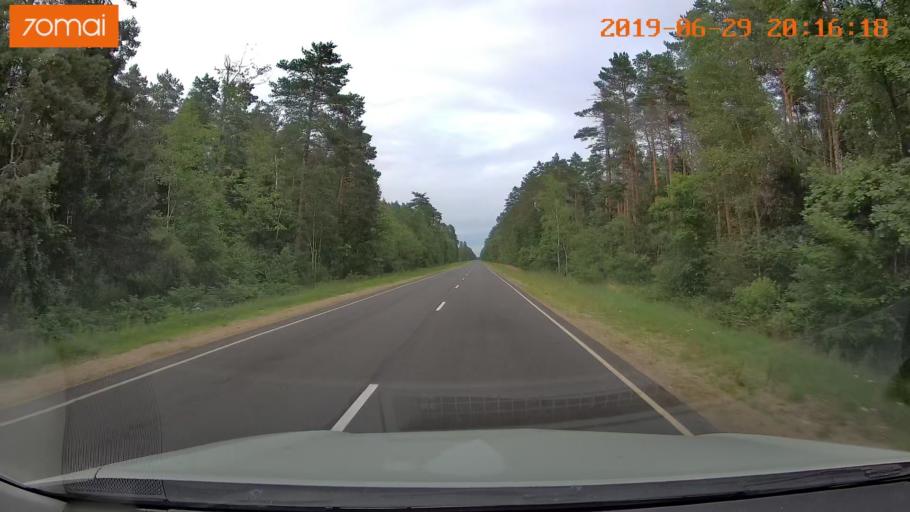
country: BY
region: Brest
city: Asnyezhytsy
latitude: 52.3802
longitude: 26.1935
